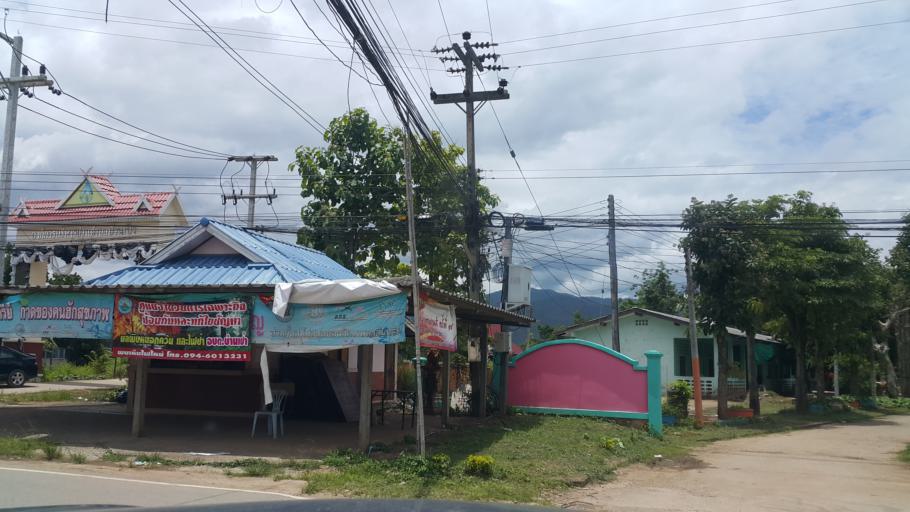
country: TH
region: Chiang Mai
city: Mae Taeng
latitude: 19.1886
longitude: 98.9967
